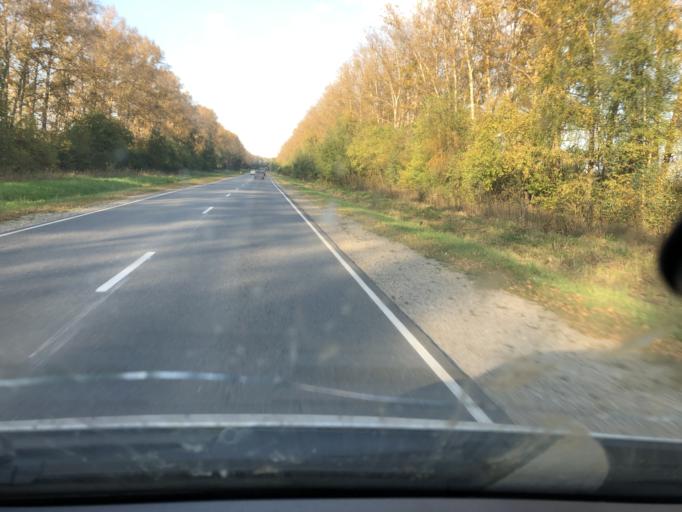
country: RU
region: Kaluga
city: Peremyshl'
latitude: 54.2363
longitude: 36.0672
